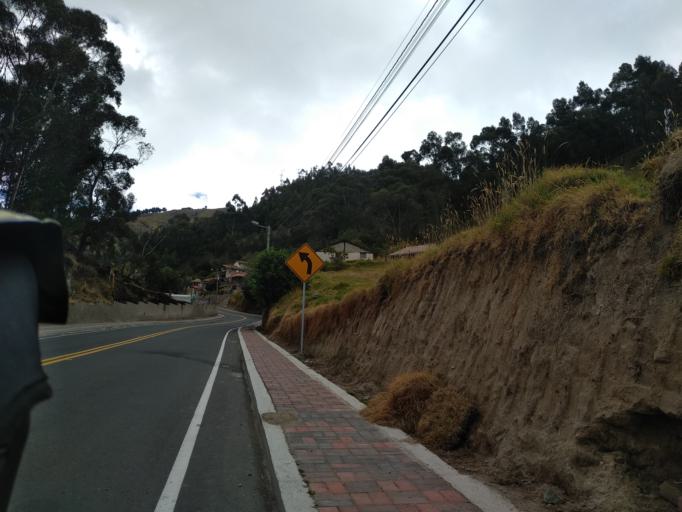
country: EC
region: Cotopaxi
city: Saquisili
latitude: -0.7988
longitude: -78.9174
